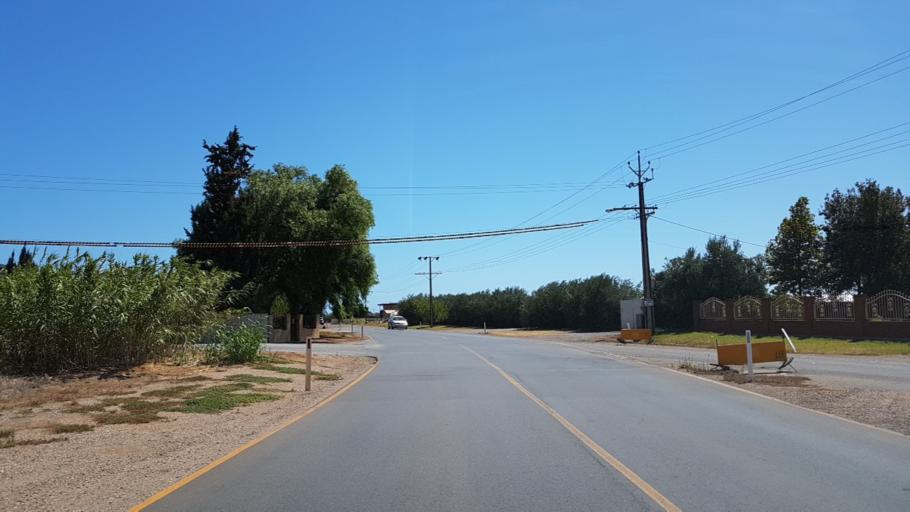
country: AU
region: South Australia
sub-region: Playford
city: Virginia
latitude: -34.7262
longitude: 138.5742
